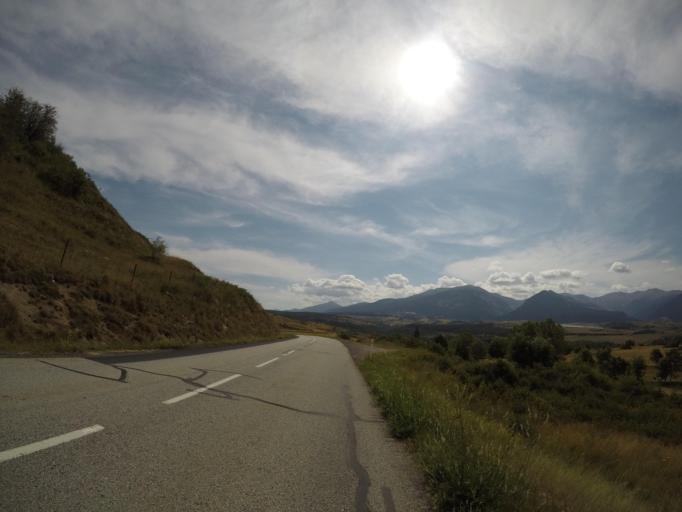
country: ES
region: Catalonia
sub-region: Provincia de Girona
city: Llivia
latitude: 42.4882
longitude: 2.0435
